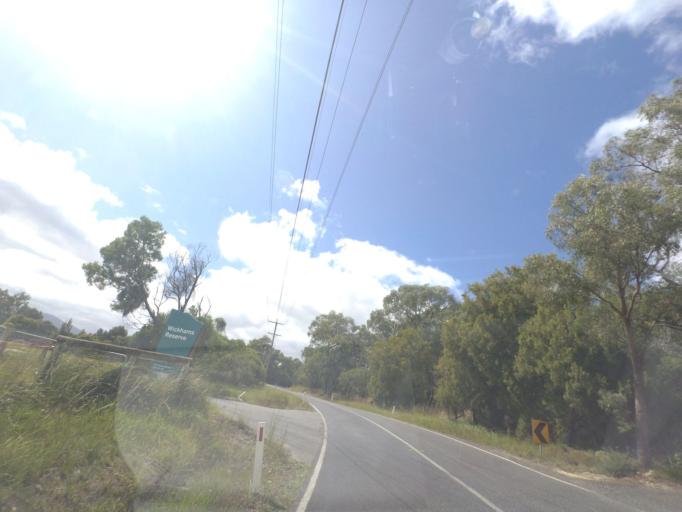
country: AU
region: Victoria
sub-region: Yarra Ranges
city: Launching Place
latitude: -37.7895
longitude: 145.5697
